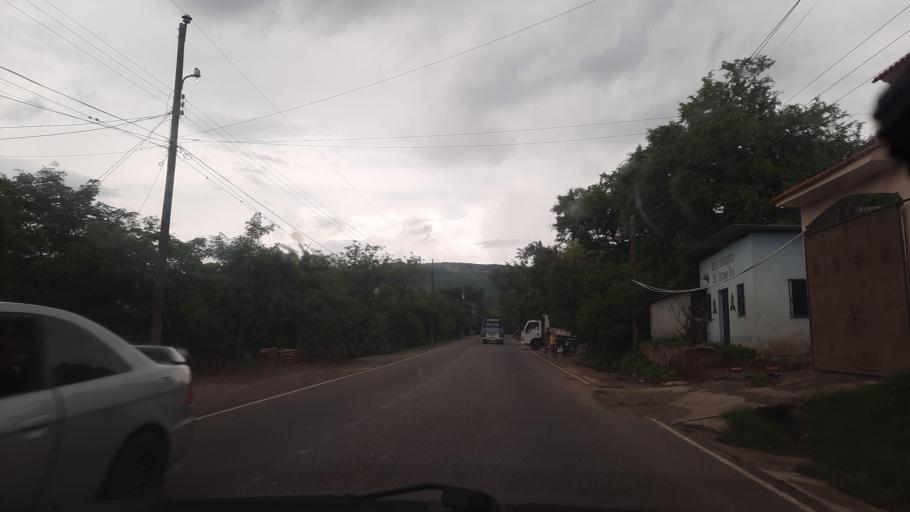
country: GT
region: Zacapa
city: San Jorge
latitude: 14.9141
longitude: -89.5296
